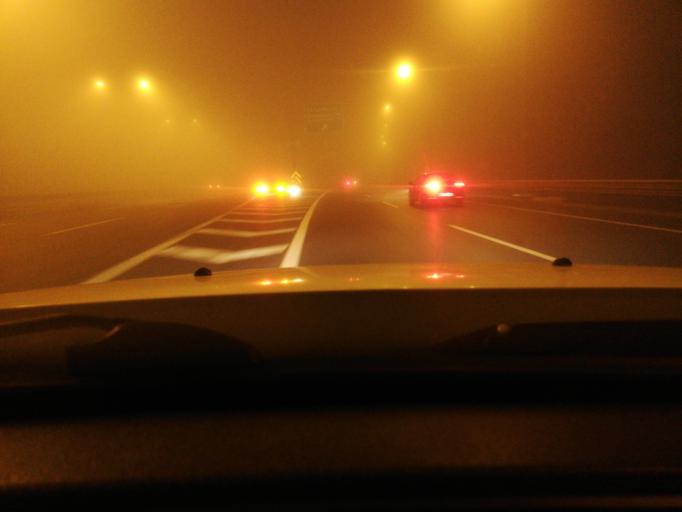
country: TR
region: Istanbul
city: Sultanbeyli
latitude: 40.9768
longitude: 29.3274
